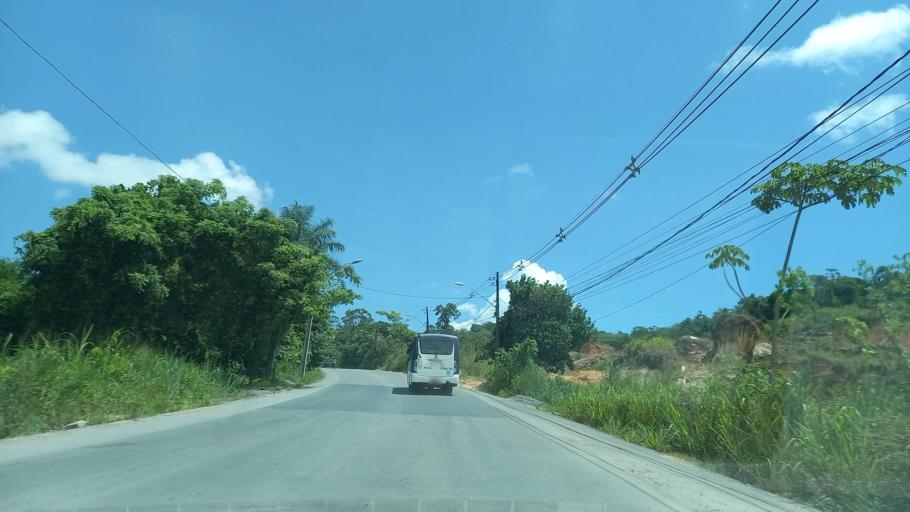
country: BR
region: Pernambuco
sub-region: Jaboatao Dos Guararapes
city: Jaboatao
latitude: -8.1620
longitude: -34.9902
